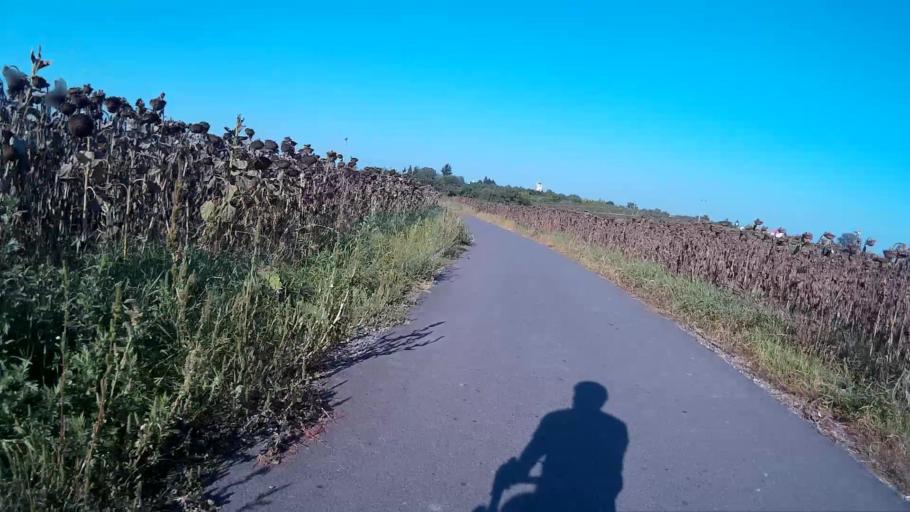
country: CZ
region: South Moravian
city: Vranovice
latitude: 48.9612
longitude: 16.5821
